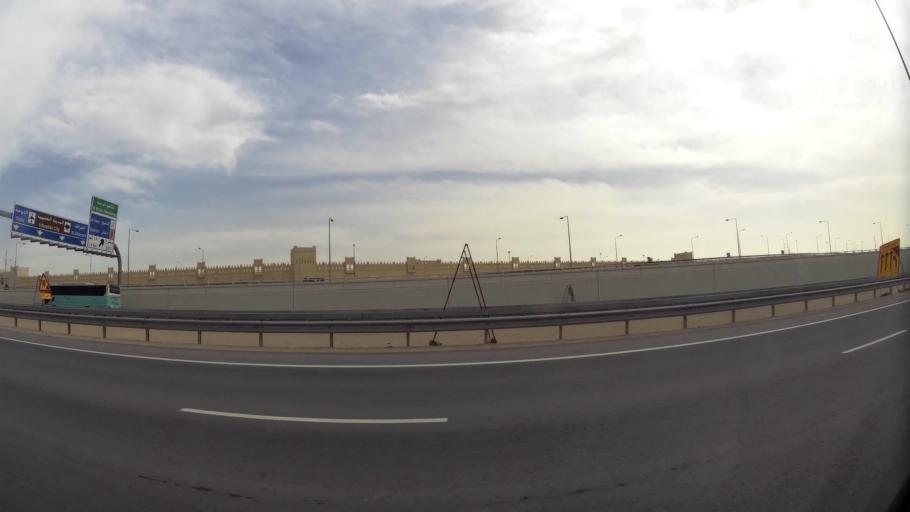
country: QA
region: Baladiyat ar Rayyan
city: Ar Rayyan
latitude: 25.3189
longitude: 51.3569
